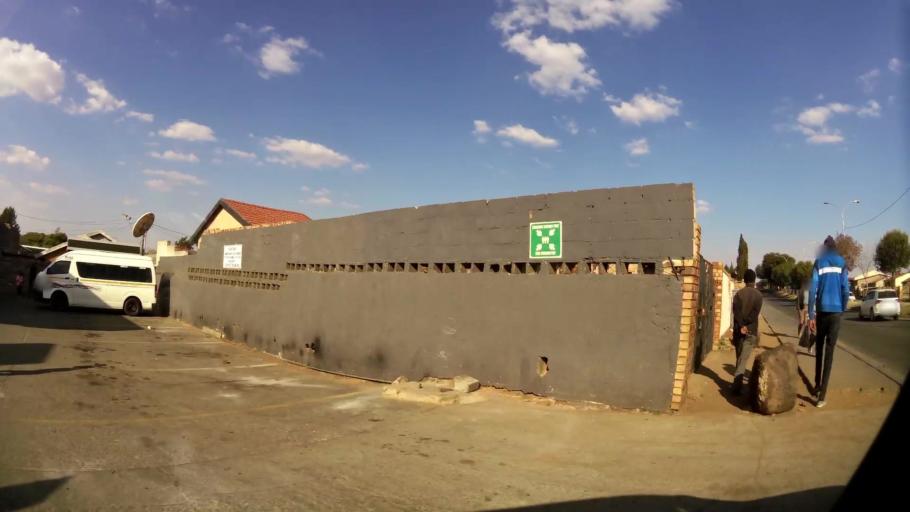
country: ZA
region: Gauteng
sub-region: City of Johannesburg Metropolitan Municipality
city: Soweto
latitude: -26.2226
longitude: 27.8726
